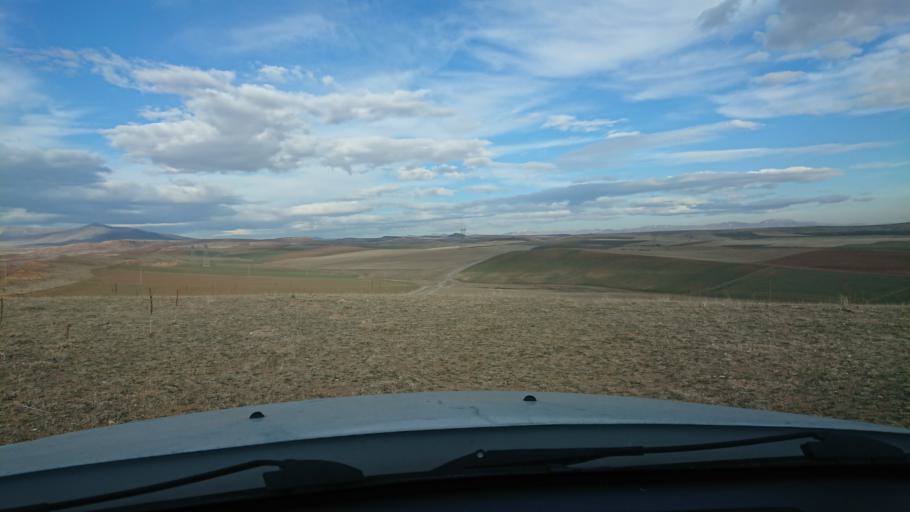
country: TR
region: Aksaray
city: Sariyahsi
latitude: 39.0523
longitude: 33.9790
